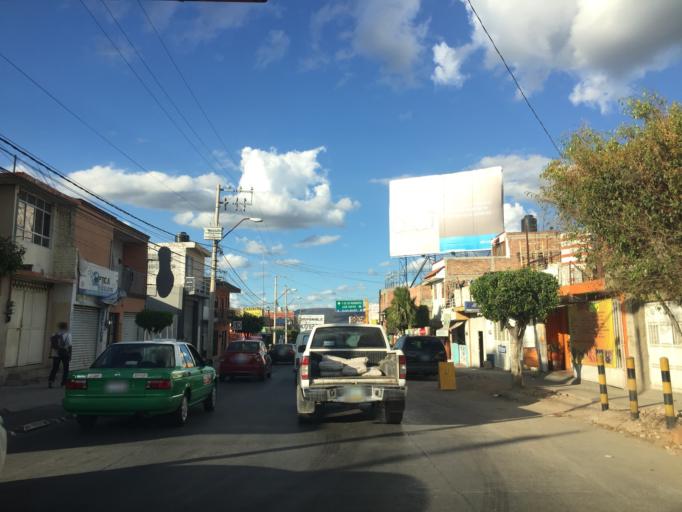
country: MX
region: Guanajuato
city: Leon
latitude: 21.1291
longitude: -101.7041
